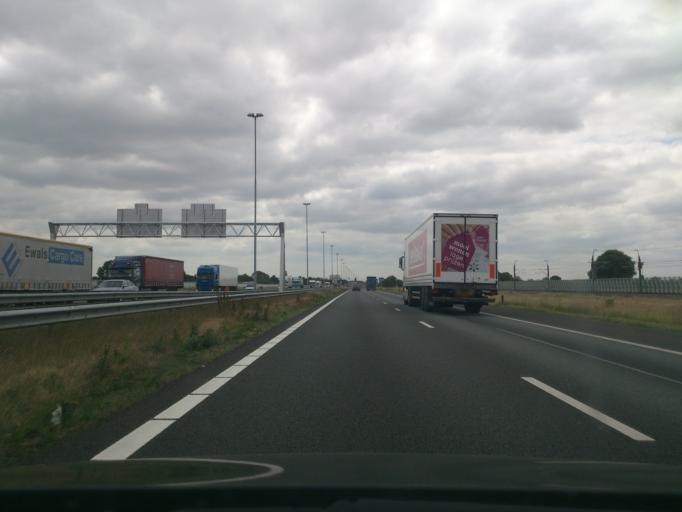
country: NL
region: North Brabant
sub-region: Gemeente Breda
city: Breda
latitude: 51.5165
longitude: 4.7452
